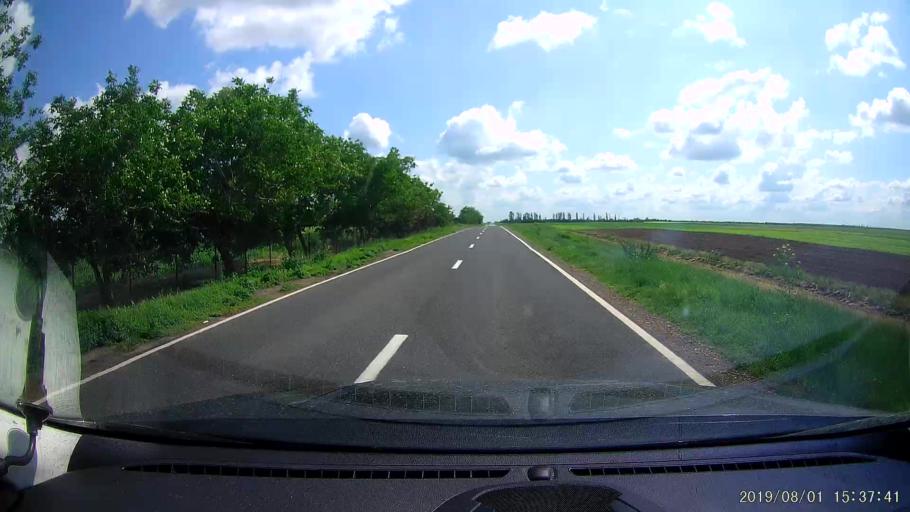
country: RO
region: Braila
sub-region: Comuna Insuratei
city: Insuratei
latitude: 44.8987
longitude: 27.5865
